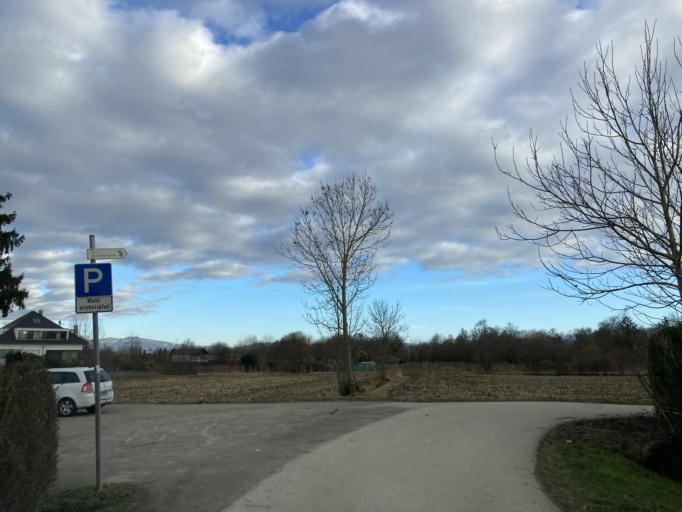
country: DE
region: Baden-Wuerttemberg
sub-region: Freiburg Region
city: Botzingen
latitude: 48.0640
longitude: 7.7101
